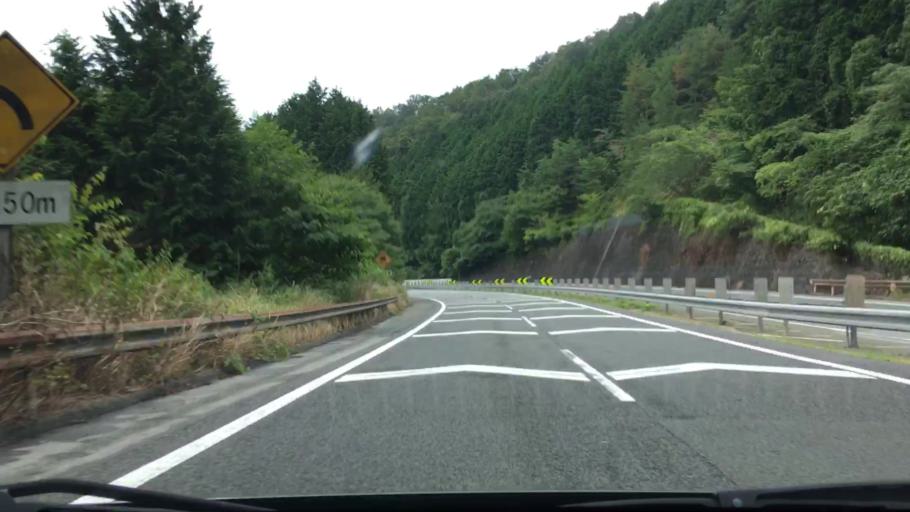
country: JP
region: Hiroshima
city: Shobara
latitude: 34.8895
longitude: 133.1978
